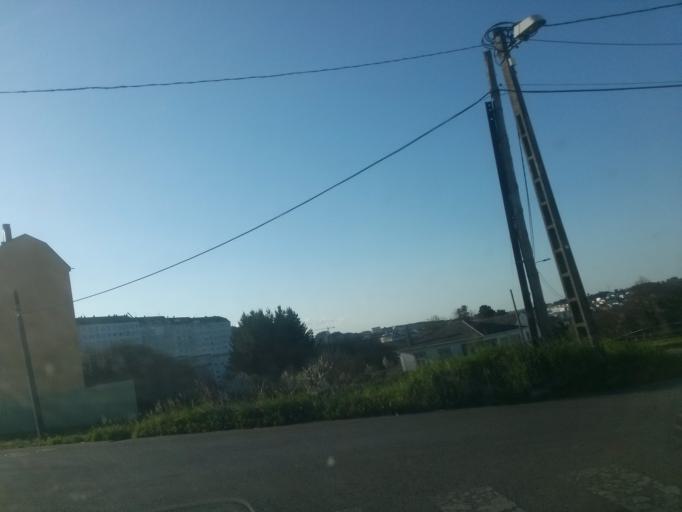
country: ES
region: Galicia
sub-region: Provincia de Lugo
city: Lugo
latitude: 43.0017
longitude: -7.5420
